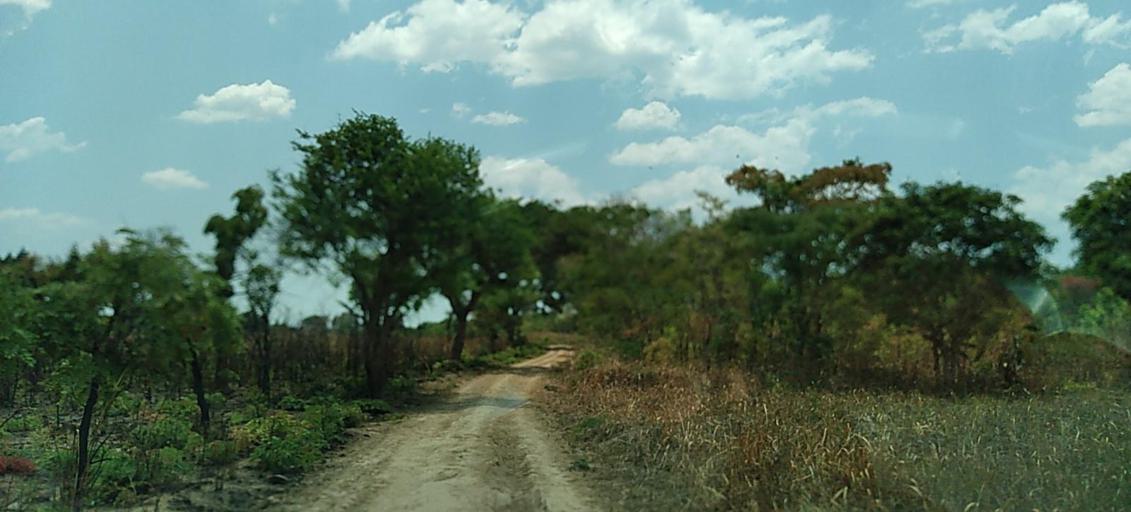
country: ZM
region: Copperbelt
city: Chililabombwe
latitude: -12.4533
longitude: 27.6747
